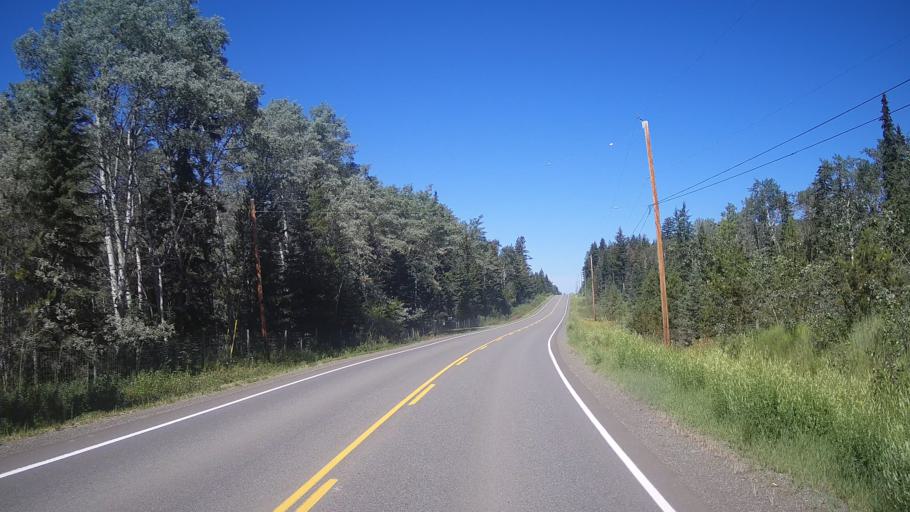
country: CA
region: British Columbia
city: Cache Creek
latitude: 51.5405
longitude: -121.0506
